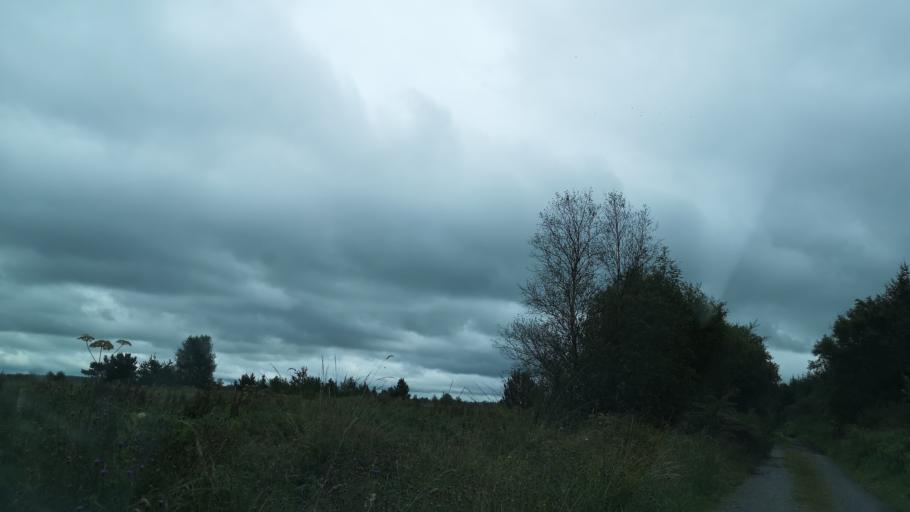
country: IE
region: Connaught
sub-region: County Galway
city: Athenry
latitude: 53.3041
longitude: -8.6608
